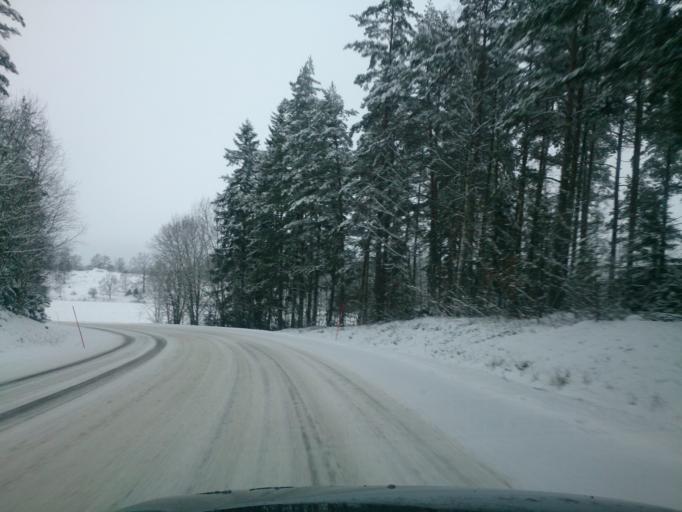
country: SE
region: OEstergoetland
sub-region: Norrkopings Kommun
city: Kimstad
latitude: 58.3770
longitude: 16.0286
